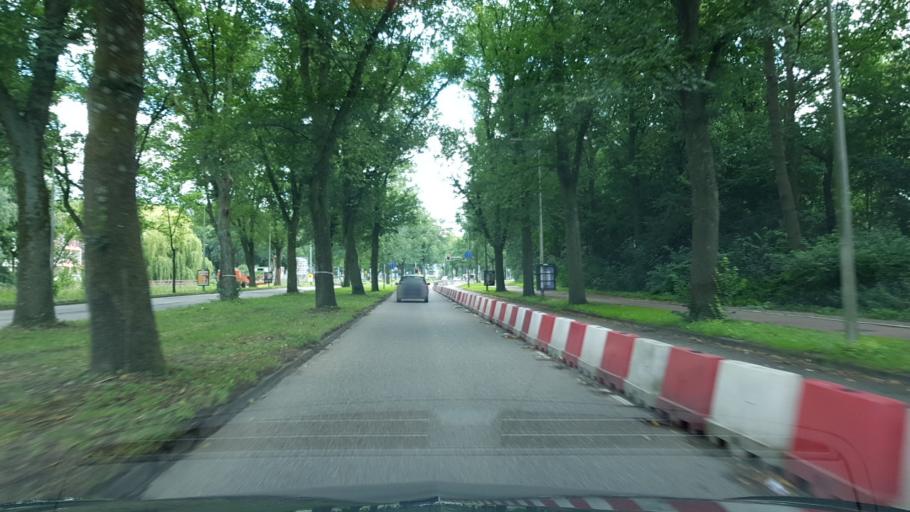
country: NL
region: Utrecht
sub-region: Gemeente Utrecht
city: Utrecht
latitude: 52.1117
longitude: 5.1090
